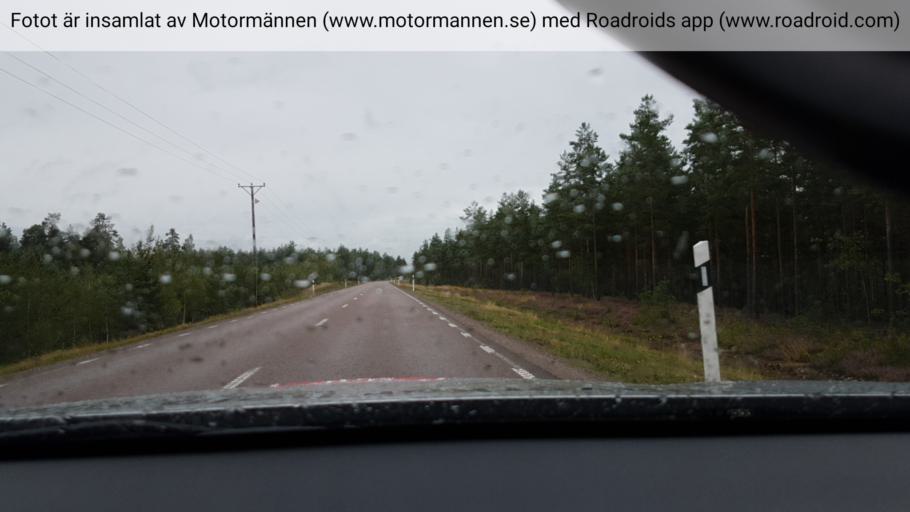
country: SE
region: Gaevleborg
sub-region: Gavle Kommun
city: Valbo
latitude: 60.5491
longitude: 16.9461
